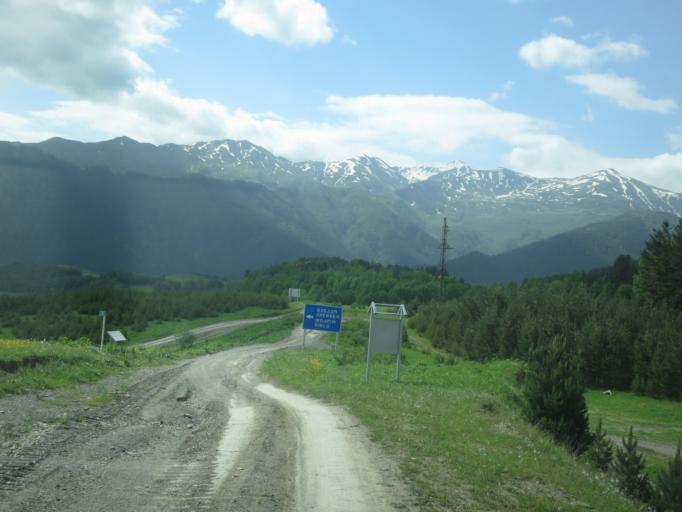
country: RU
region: Chechnya
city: Itum-Kali
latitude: 42.3696
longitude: 45.6262
